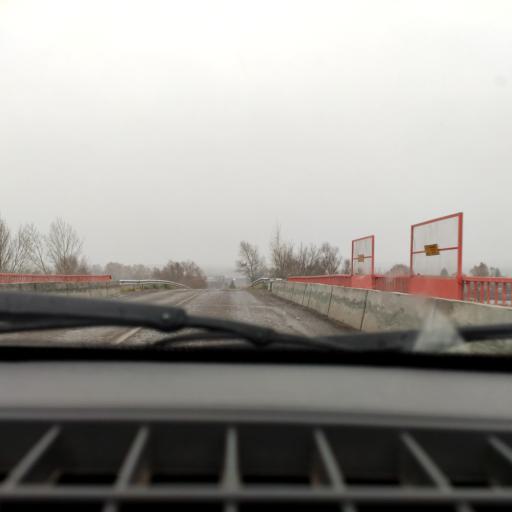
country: RU
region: Bashkortostan
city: Avdon
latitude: 54.6519
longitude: 55.7778
